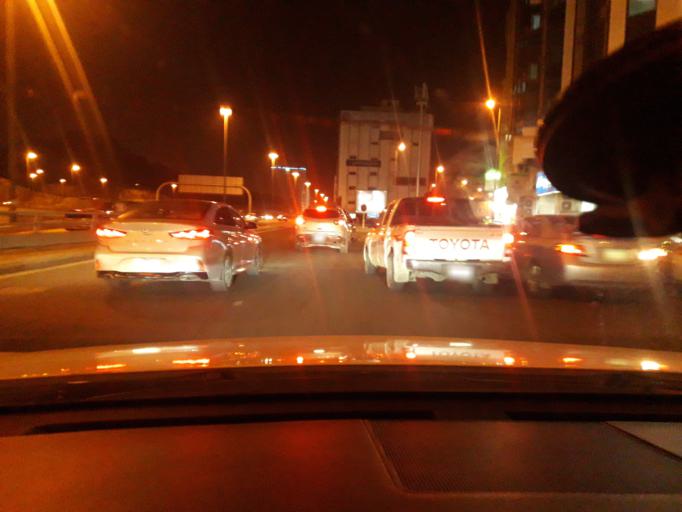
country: SA
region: Al Madinah al Munawwarah
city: Medina
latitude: 24.4762
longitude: 39.6052
